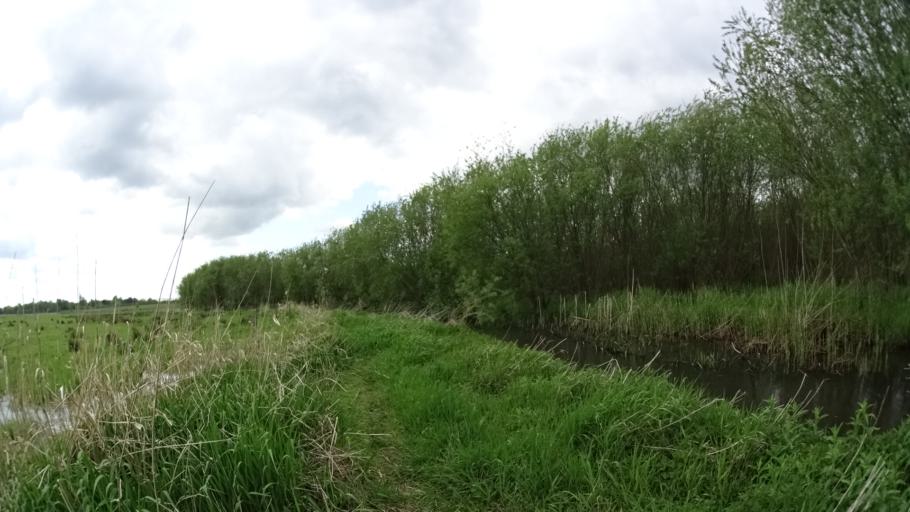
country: DK
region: Central Jutland
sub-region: Arhus Kommune
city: Kolt
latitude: 56.1412
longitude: 10.0632
